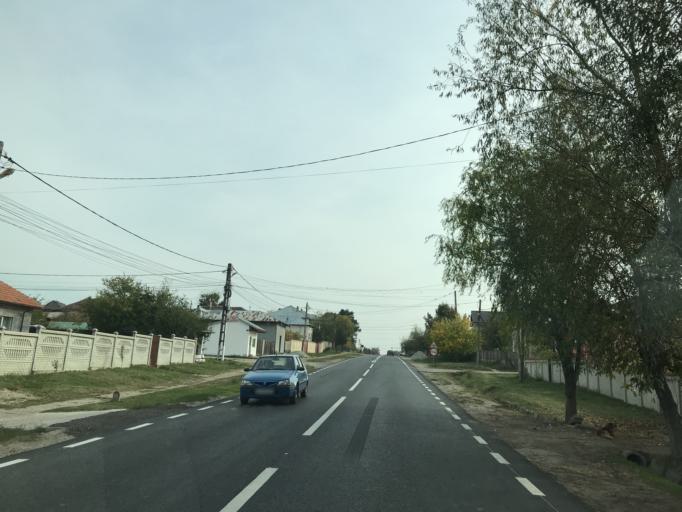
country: RO
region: Olt
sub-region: Comuna Piatra Olt
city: Piatra
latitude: 44.3628
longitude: 24.2933
